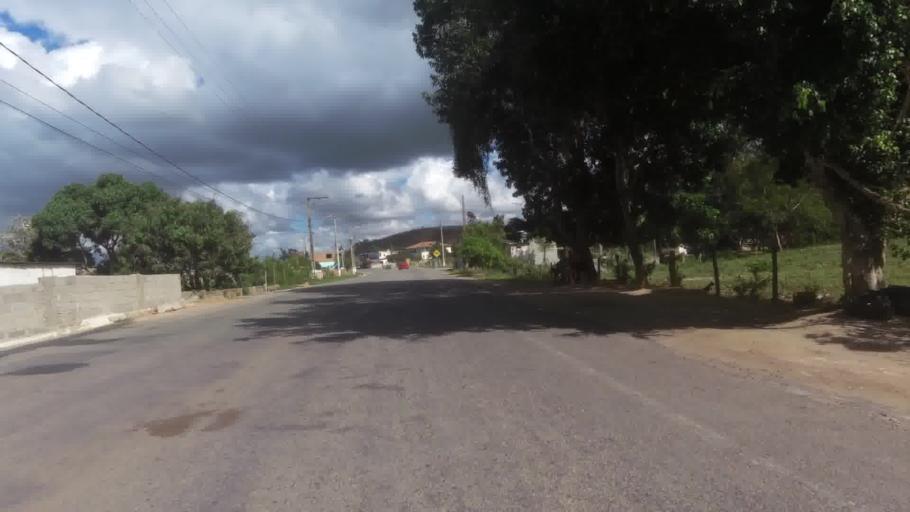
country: BR
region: Espirito Santo
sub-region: Marataizes
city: Marataizes
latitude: -21.1994
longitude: -40.9613
